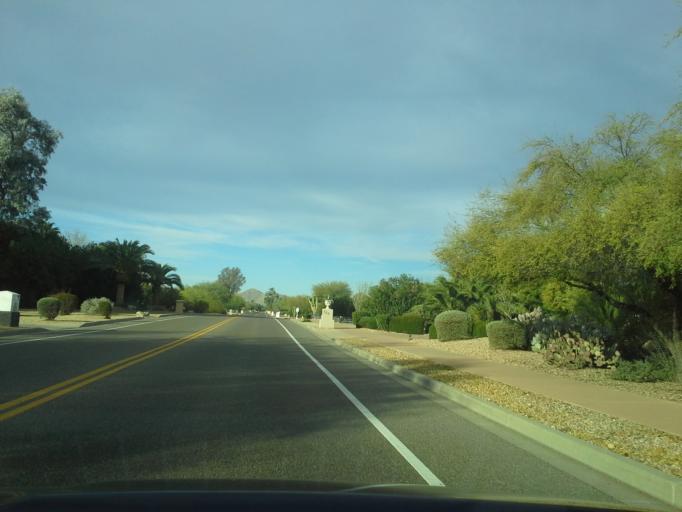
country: US
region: Arizona
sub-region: Maricopa County
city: Paradise Valley
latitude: 33.5675
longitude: -111.9281
